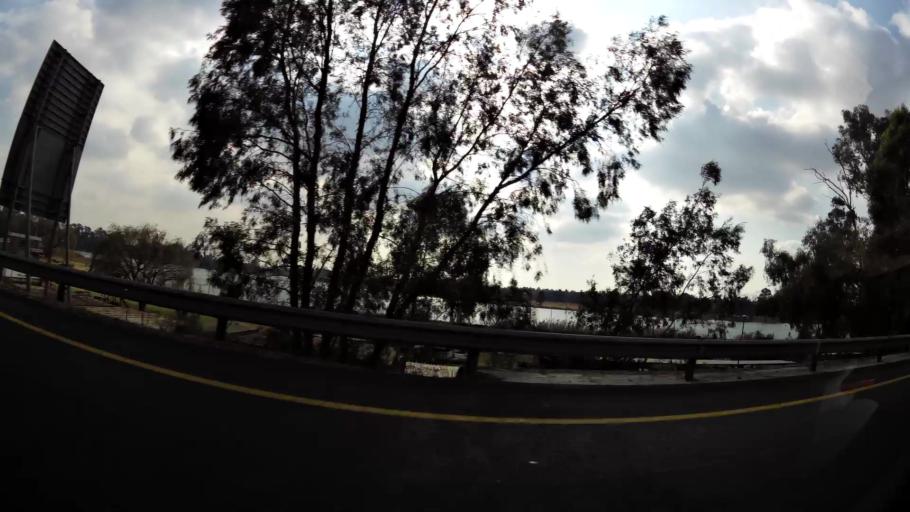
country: ZA
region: Gauteng
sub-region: Ekurhuleni Metropolitan Municipality
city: Benoni
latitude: -26.1747
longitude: 28.2879
